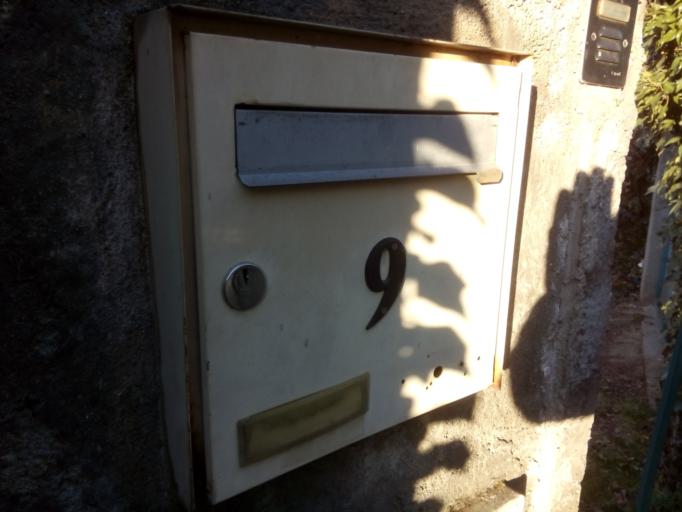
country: FR
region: Ile-de-France
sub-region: Departement des Hauts-de-Seine
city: Vanves
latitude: 48.8151
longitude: 2.2927
